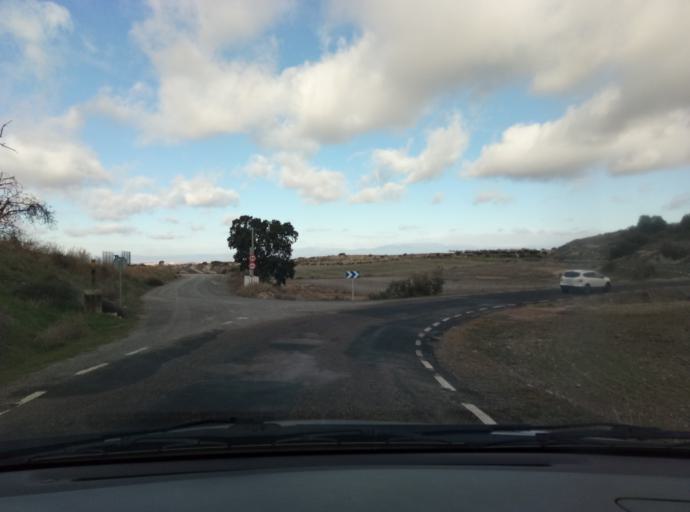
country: ES
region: Catalonia
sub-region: Provincia de Lleida
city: Nalec
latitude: 41.5905
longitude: 1.0843
